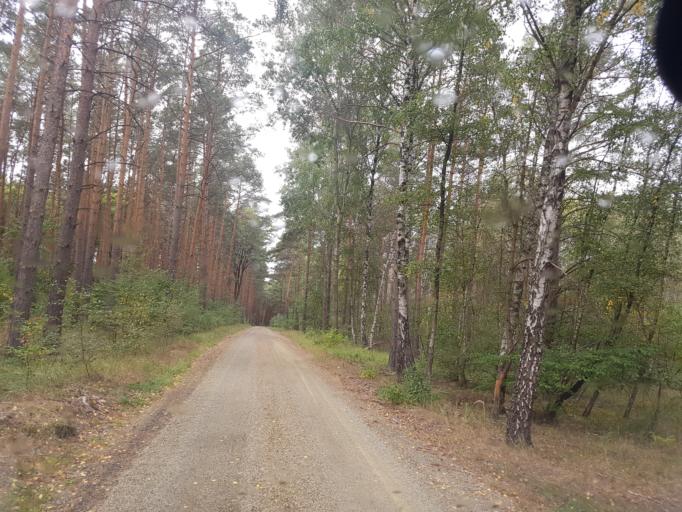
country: DE
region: Brandenburg
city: Schonborn
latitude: 51.5771
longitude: 13.4663
